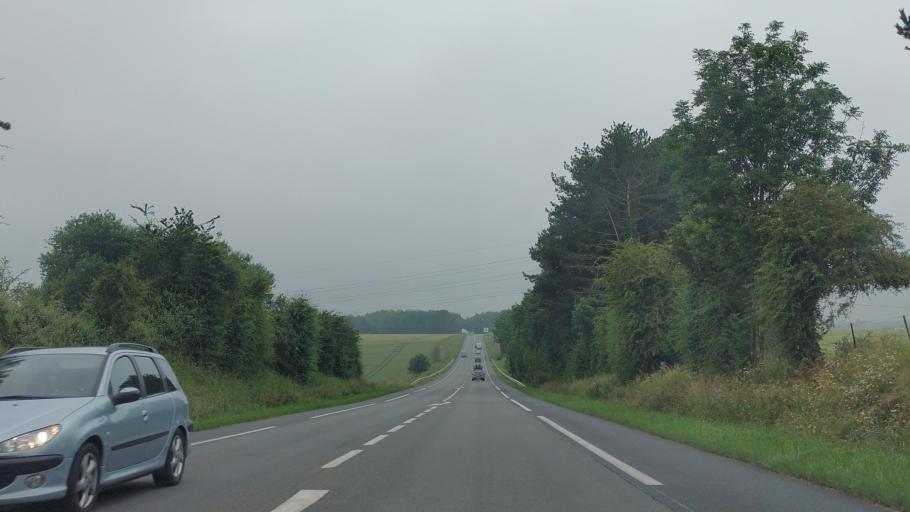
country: FR
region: Picardie
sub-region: Departement de la Somme
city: Fressenneville
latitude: 50.0740
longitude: 1.5701
